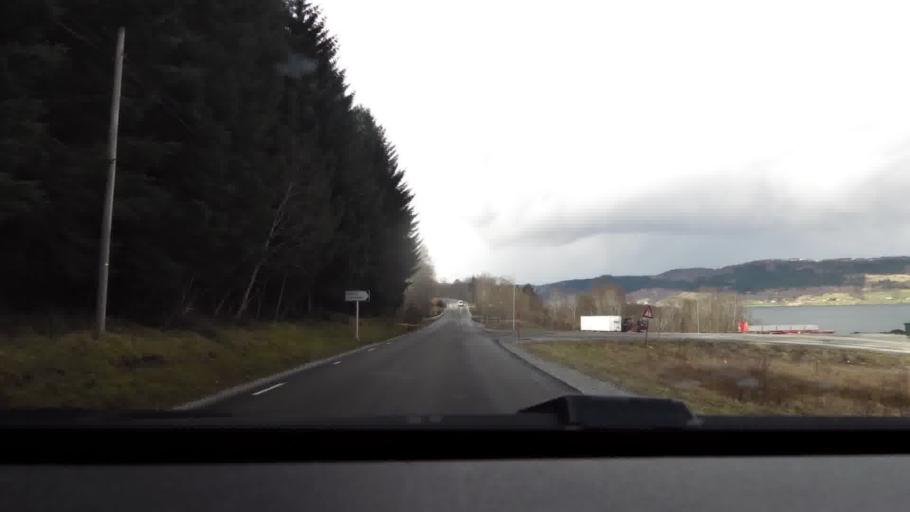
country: NO
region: More og Romsdal
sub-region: Gjemnes
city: Batnfjordsora
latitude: 62.9676
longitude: 7.7299
